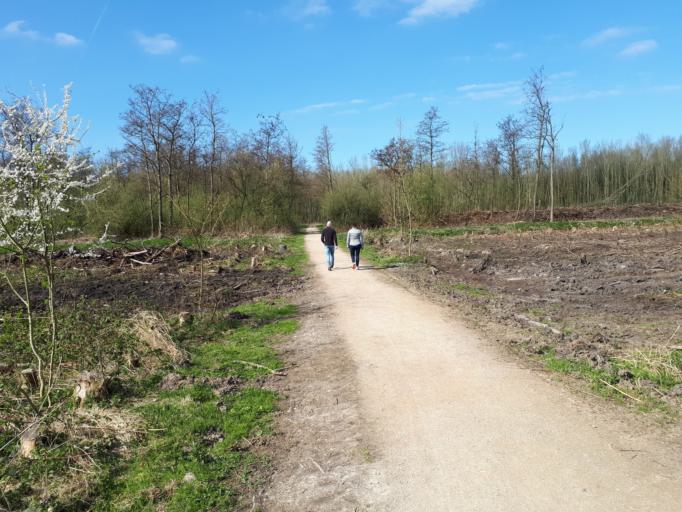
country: NL
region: South Holland
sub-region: Gemeente Pijnacker-Nootdorp
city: Pijnacker
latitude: 52.0242
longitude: 4.4084
